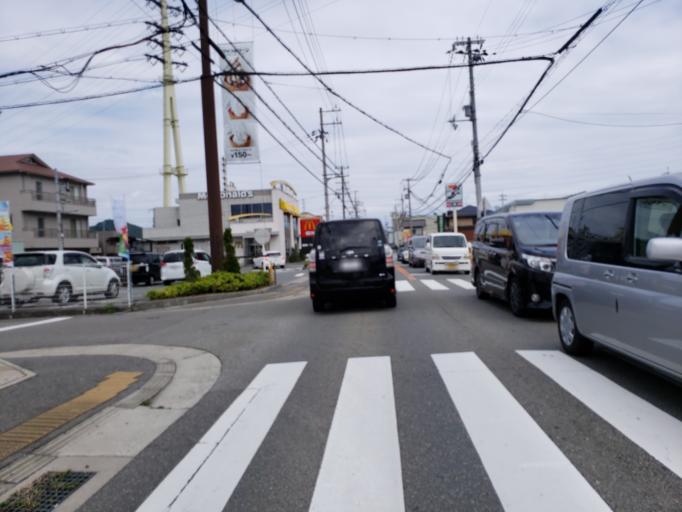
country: JP
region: Hyogo
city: Himeji
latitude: 34.7934
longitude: 134.6819
